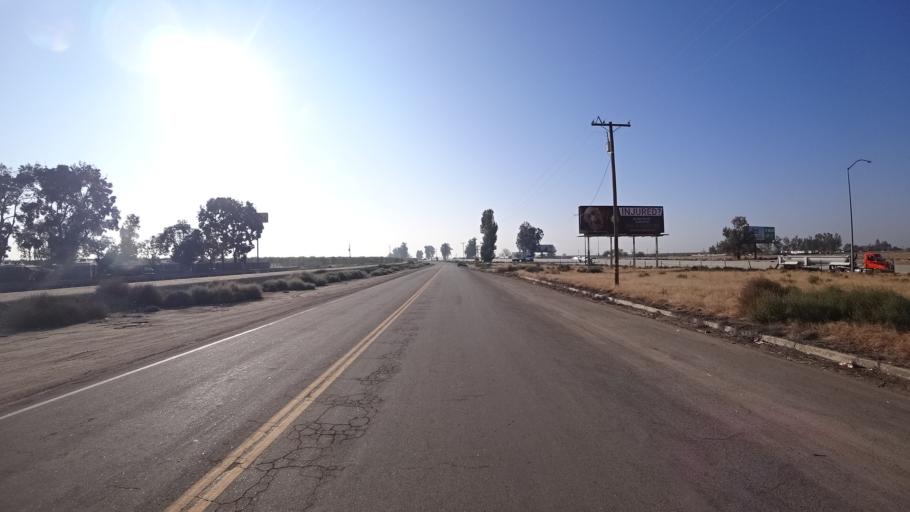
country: US
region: California
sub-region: Kern County
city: Greenfield
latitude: 35.2639
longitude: -119.0213
